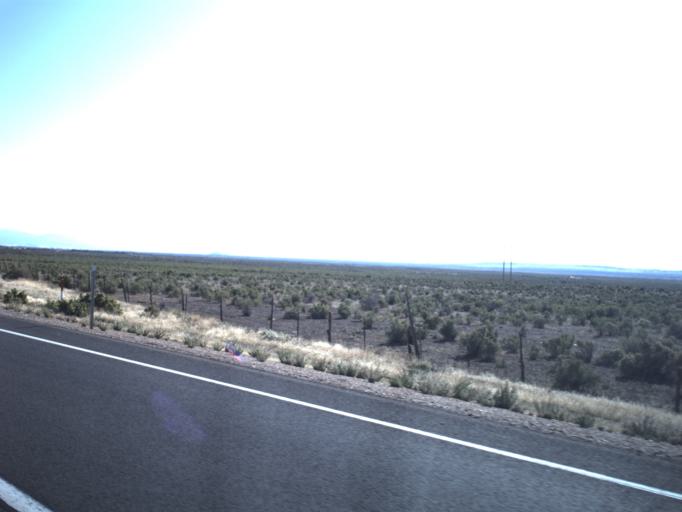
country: US
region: Utah
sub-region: Millard County
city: Fillmore
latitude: 39.1582
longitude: -112.4099
